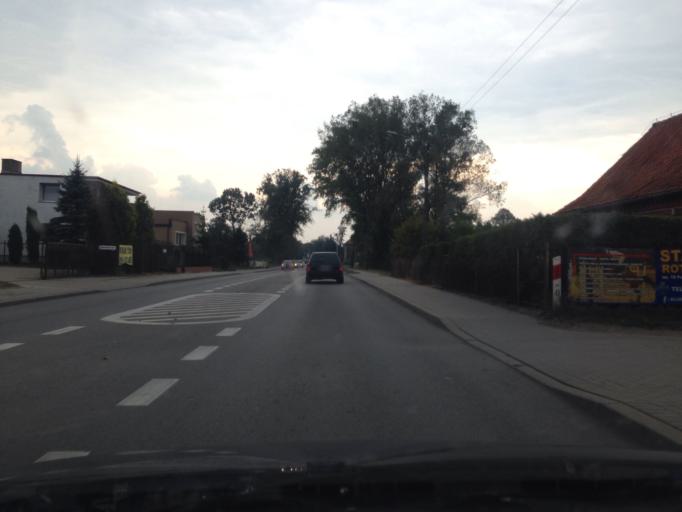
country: PL
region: Pomeranian Voivodeship
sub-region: Powiat malborski
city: Malbork
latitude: 53.9809
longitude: 19.0016
